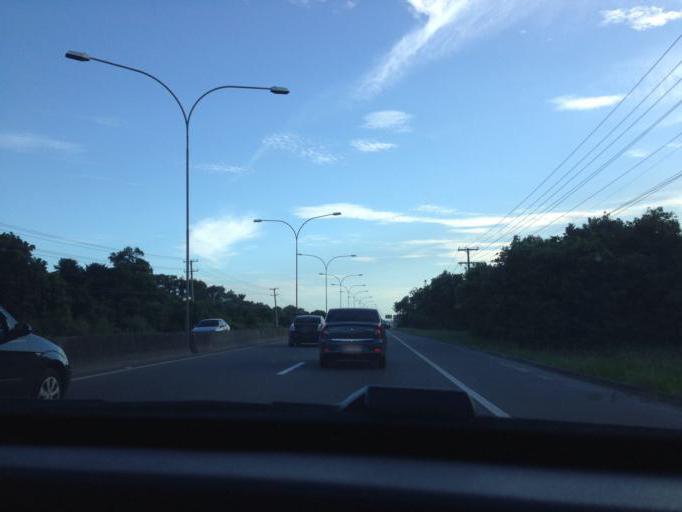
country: BR
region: Espirito Santo
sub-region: Vila Velha
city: Vila Velha
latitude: -20.4132
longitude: -40.3277
